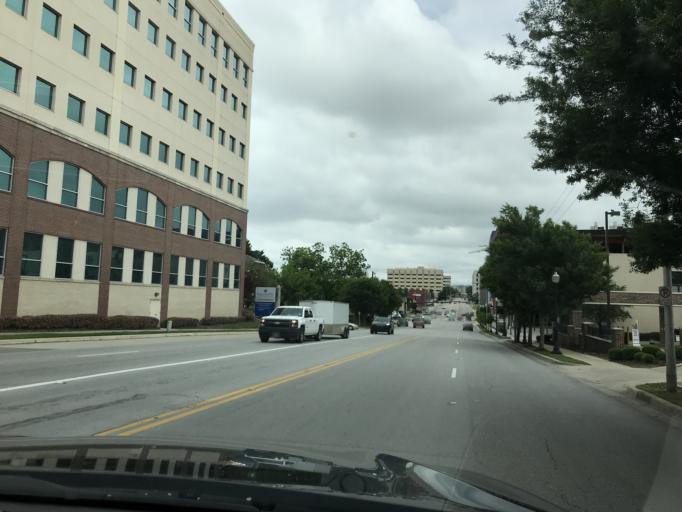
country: US
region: Texas
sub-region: Tarrant County
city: Fort Worth
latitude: 32.7310
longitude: -97.3436
